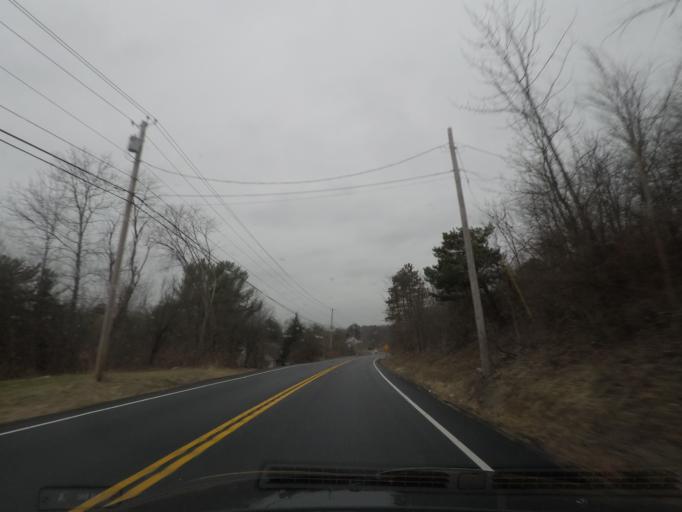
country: US
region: New York
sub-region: Rensselaer County
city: East Greenbush
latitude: 42.6185
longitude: -73.6794
